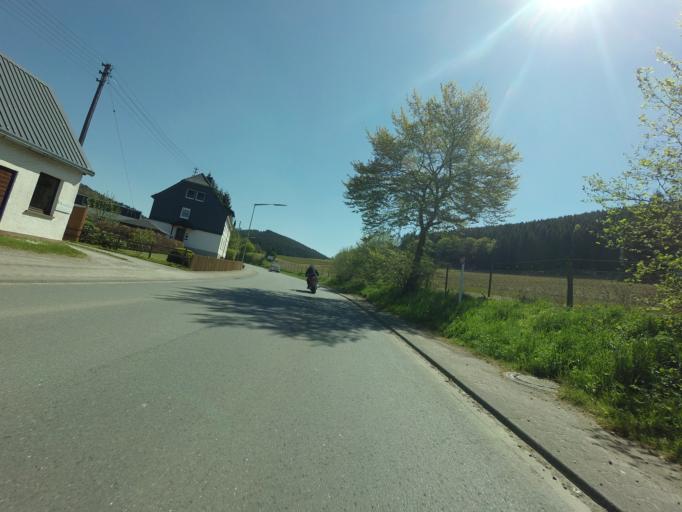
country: DE
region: North Rhine-Westphalia
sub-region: Regierungsbezirk Arnsberg
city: Kirchhundem
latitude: 51.0839
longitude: 8.1243
